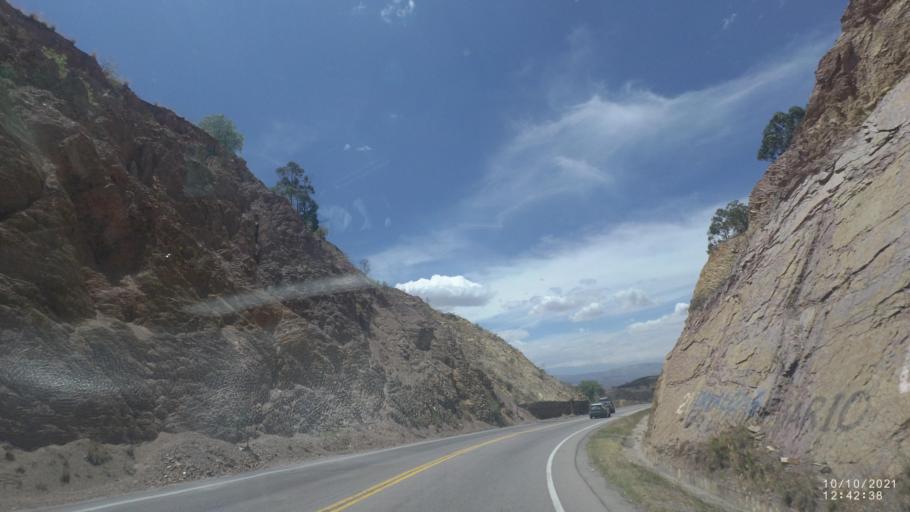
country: BO
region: Cochabamba
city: Irpa Irpa
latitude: -17.6278
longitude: -66.3936
